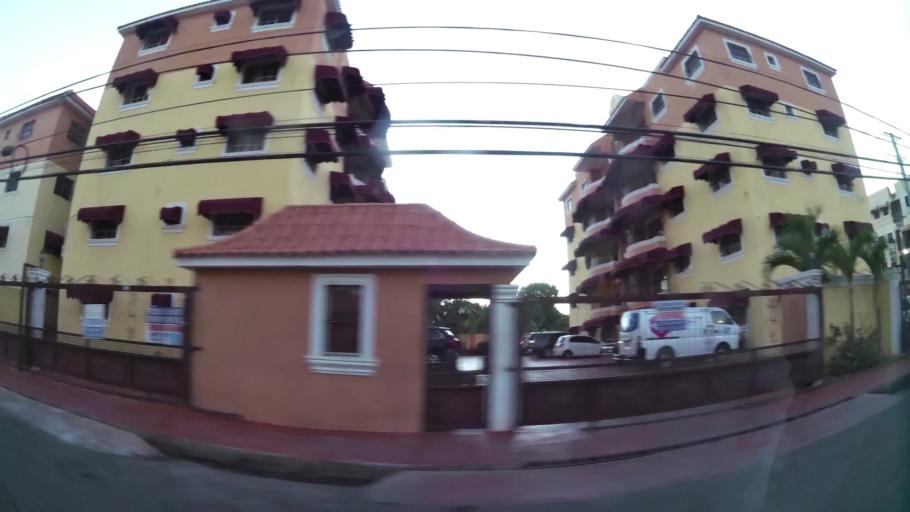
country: DO
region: Santo Domingo
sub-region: Santo Domingo
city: Santo Domingo Este
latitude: 18.4932
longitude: -69.8396
